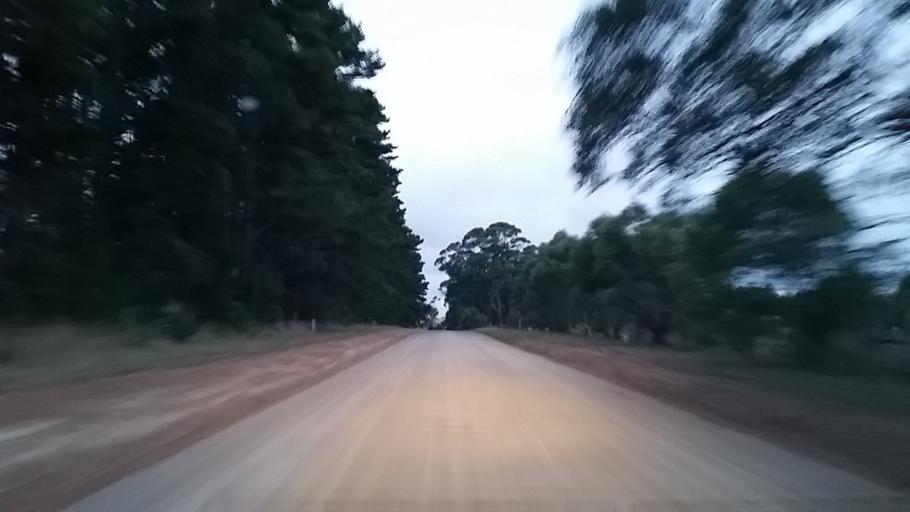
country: AU
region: South Australia
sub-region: Yankalilla
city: Normanville
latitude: -35.6098
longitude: 138.1901
